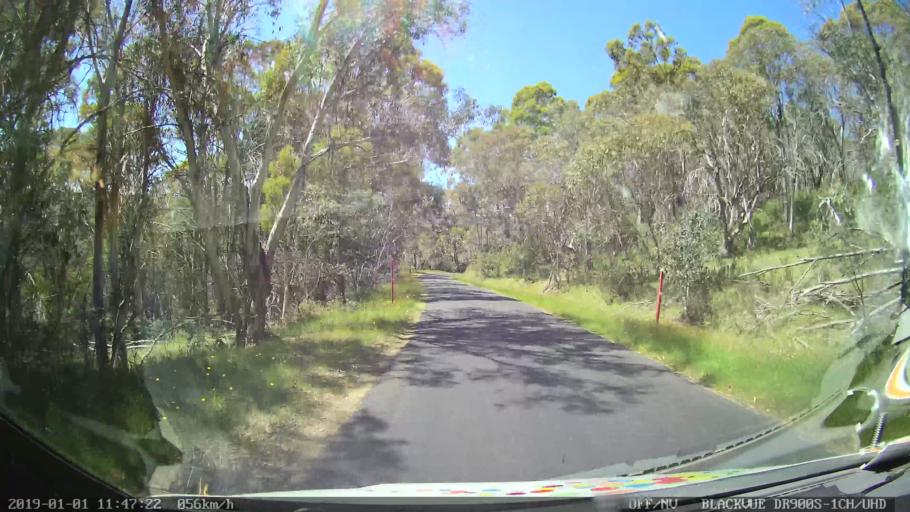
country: AU
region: New South Wales
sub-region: Snowy River
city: Jindabyne
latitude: -35.8909
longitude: 148.4038
